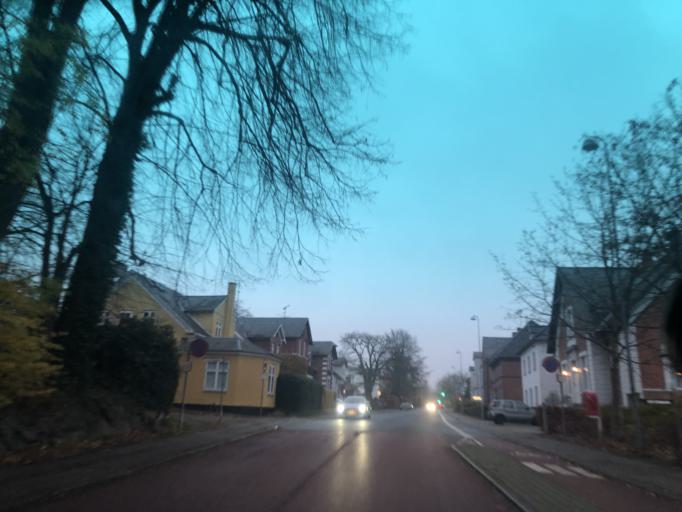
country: DK
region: South Denmark
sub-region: Svendborg Kommune
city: Svendborg
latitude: 55.0558
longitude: 10.6015
